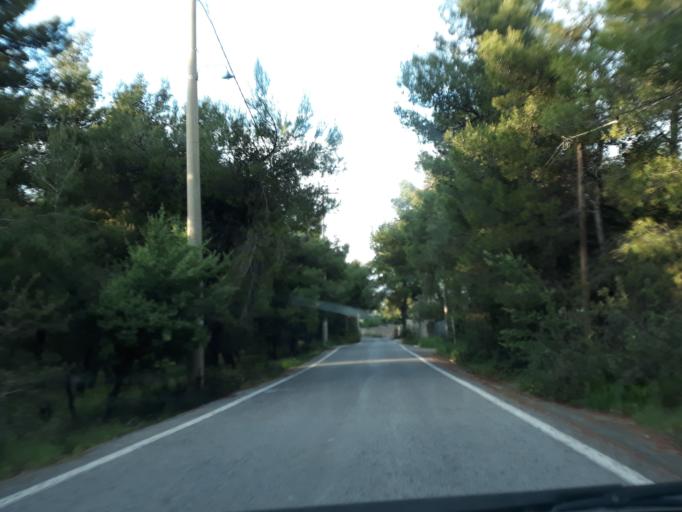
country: GR
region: Attica
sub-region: Nomarchia Anatolikis Attikis
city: Afidnes
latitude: 38.2324
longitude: 23.7876
